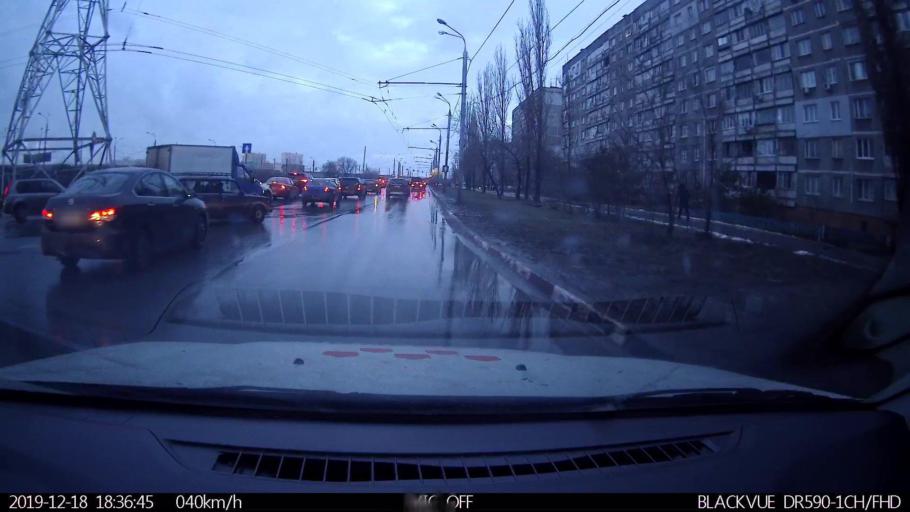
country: RU
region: Nizjnij Novgorod
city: Nizhniy Novgorod
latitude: 56.3375
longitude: 43.9258
